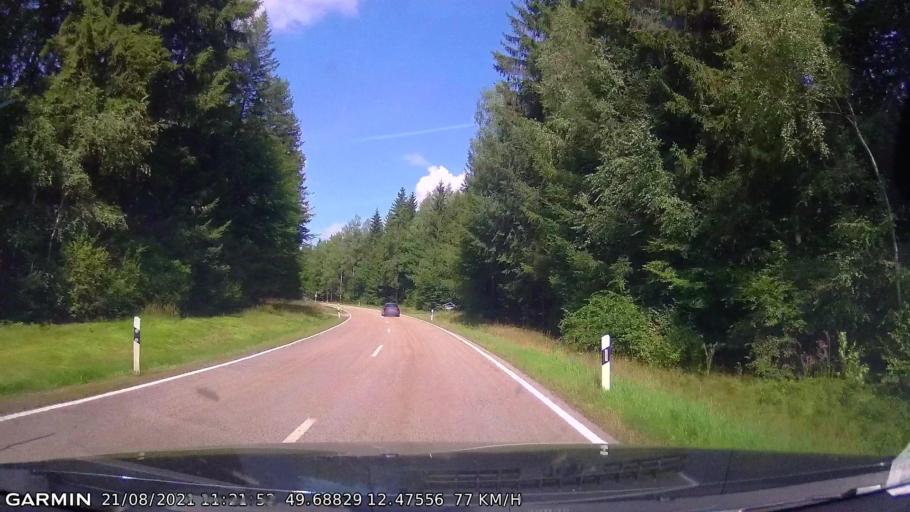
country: DE
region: Bavaria
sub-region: Upper Palatinate
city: Waidhaus
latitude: 49.6883
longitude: 12.4755
